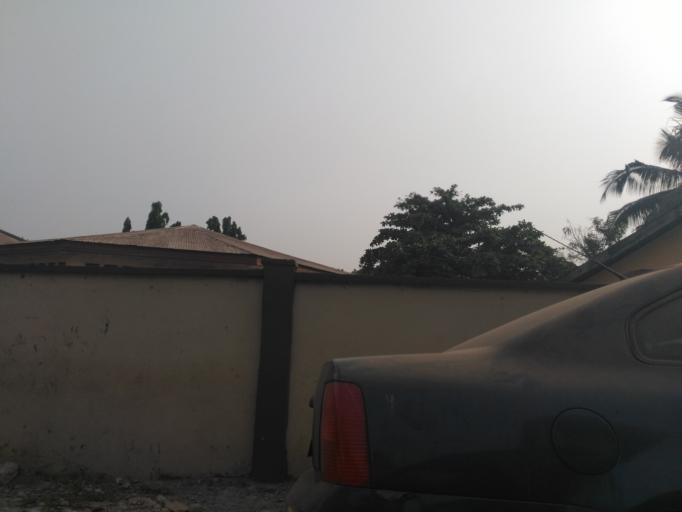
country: GH
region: Ashanti
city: Kumasi
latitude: 6.6877
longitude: -1.6091
